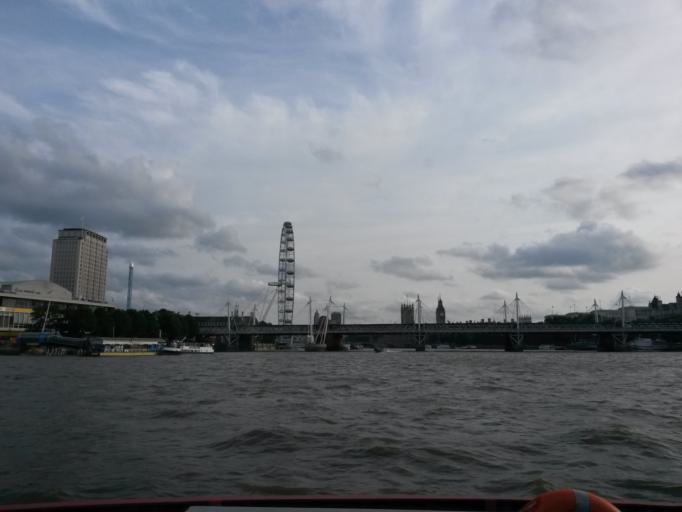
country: GB
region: England
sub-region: Greater London
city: London
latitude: 51.5087
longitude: -0.1179
